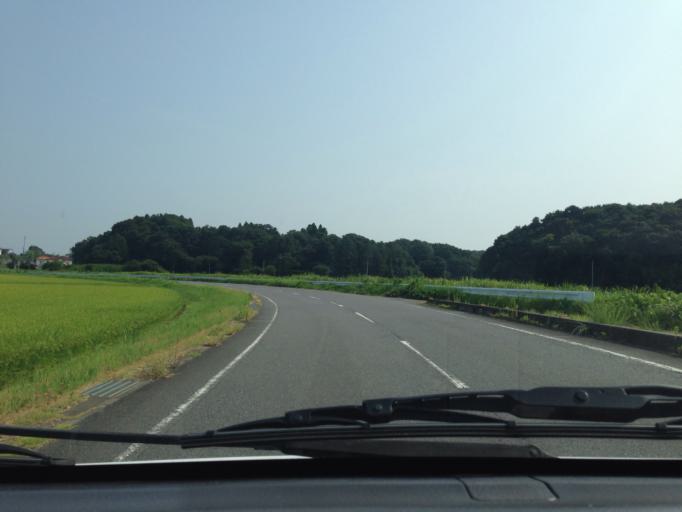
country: JP
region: Ibaraki
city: Ami
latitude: 36.0230
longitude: 140.2726
